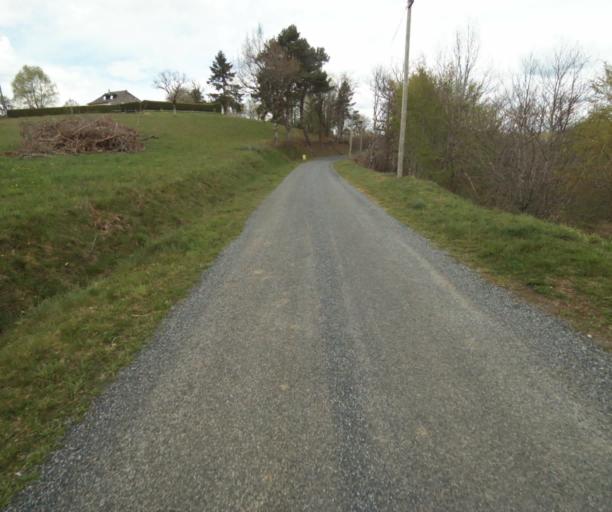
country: FR
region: Limousin
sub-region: Departement de la Correze
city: Sainte-Fortunade
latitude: 45.1957
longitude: 1.8584
